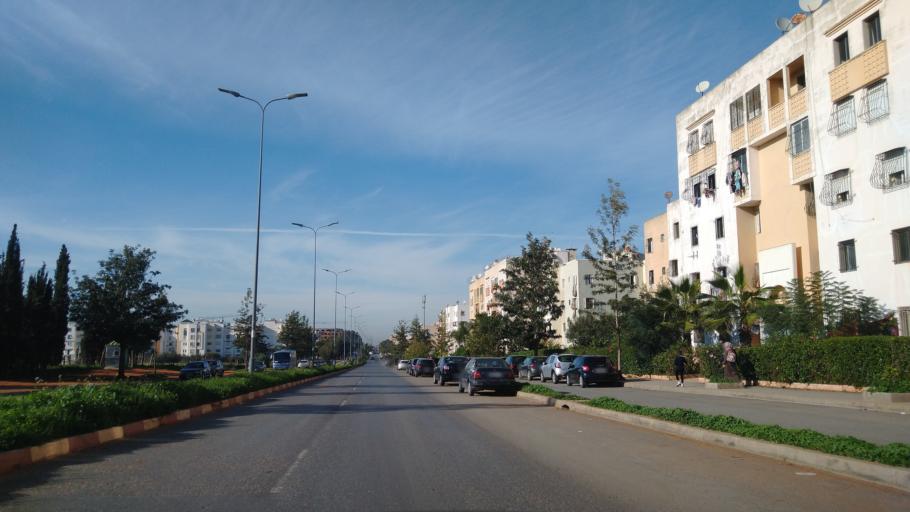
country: MA
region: Rabat-Sale-Zemmour-Zaer
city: Sale
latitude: 33.9913
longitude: -6.7419
